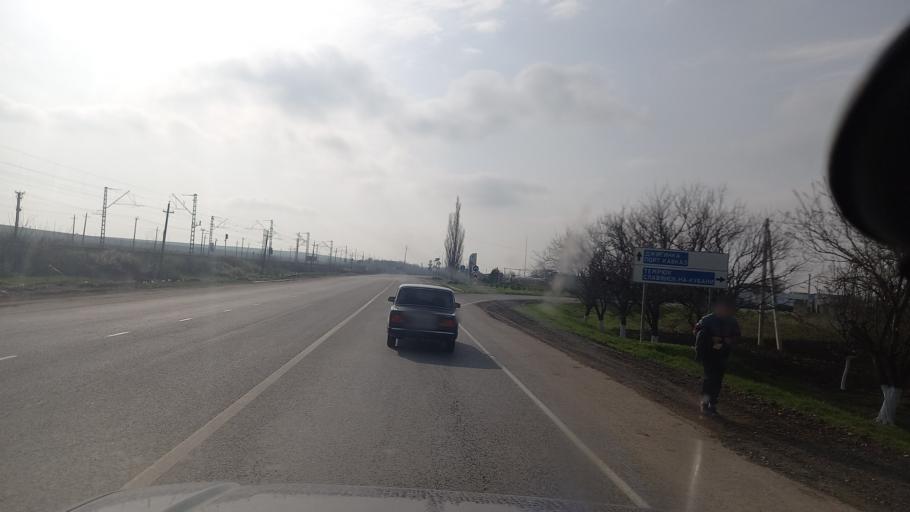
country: RU
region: Krasnodarskiy
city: Varenikovskaya
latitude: 45.1137
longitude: 37.6209
